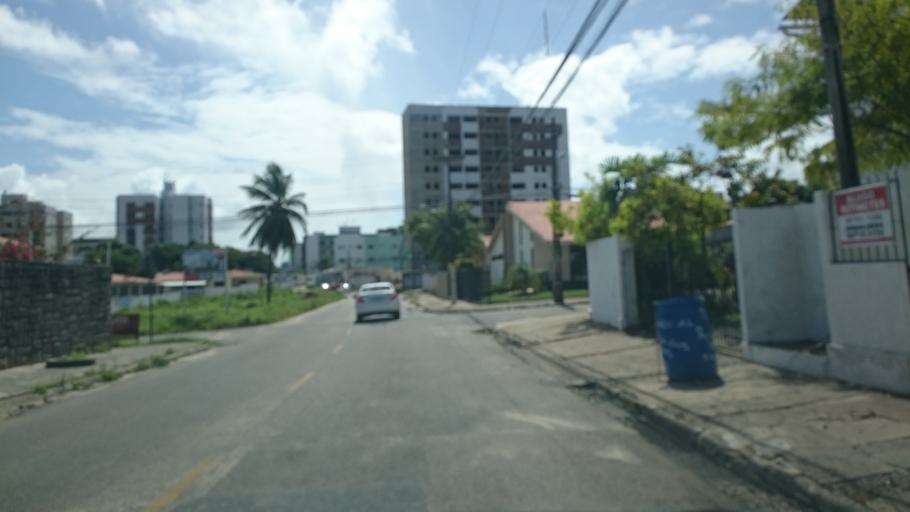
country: BR
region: Paraiba
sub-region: Joao Pessoa
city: Joao Pessoa
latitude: -7.1539
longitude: -34.8415
